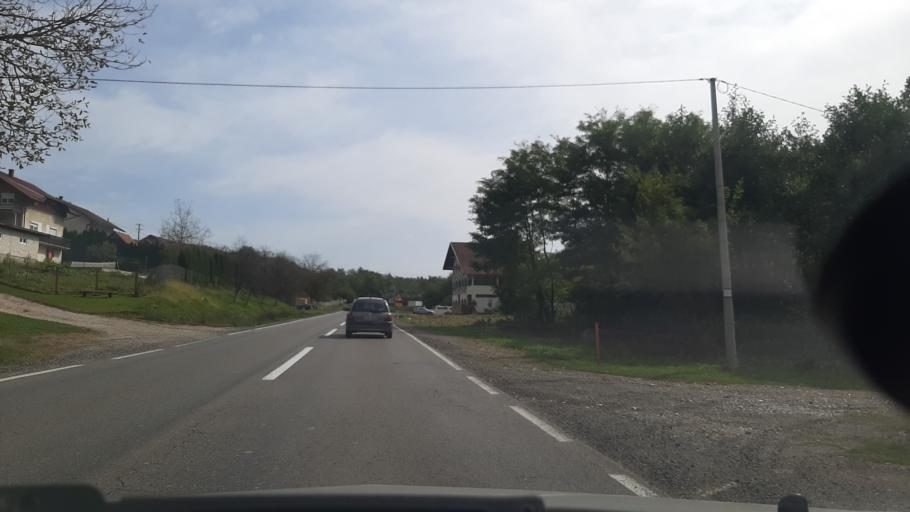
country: BA
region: Republika Srpska
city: Laktasi
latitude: 44.8735
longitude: 17.3293
